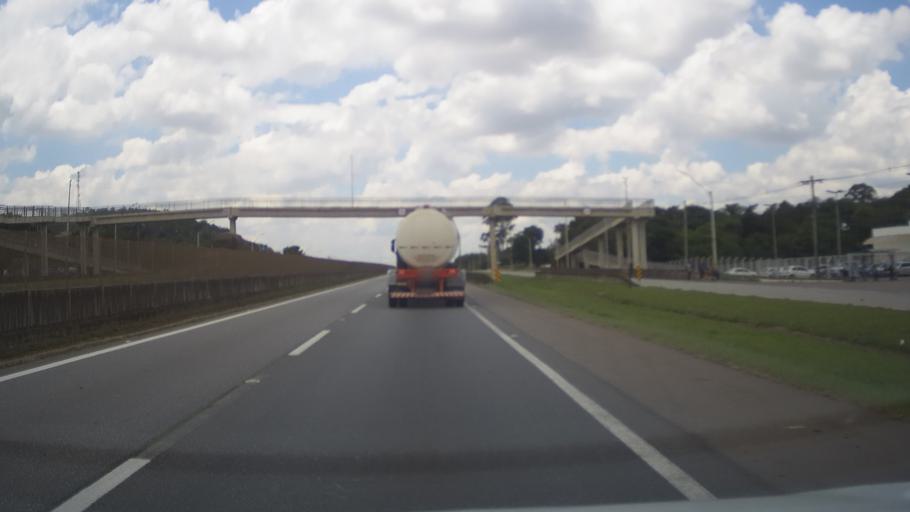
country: BR
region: Minas Gerais
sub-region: Tres Coracoes
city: Tres Coracoes
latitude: -21.6678
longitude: -45.3207
